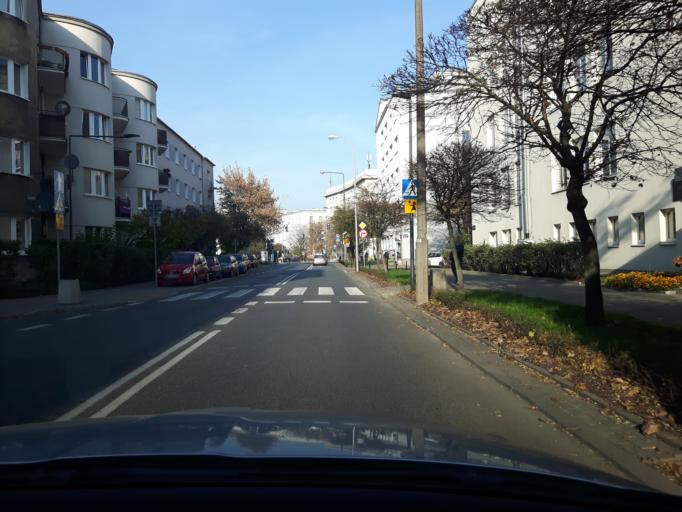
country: PL
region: Masovian Voivodeship
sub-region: Warszawa
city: Ochota
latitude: 52.2167
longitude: 20.9765
